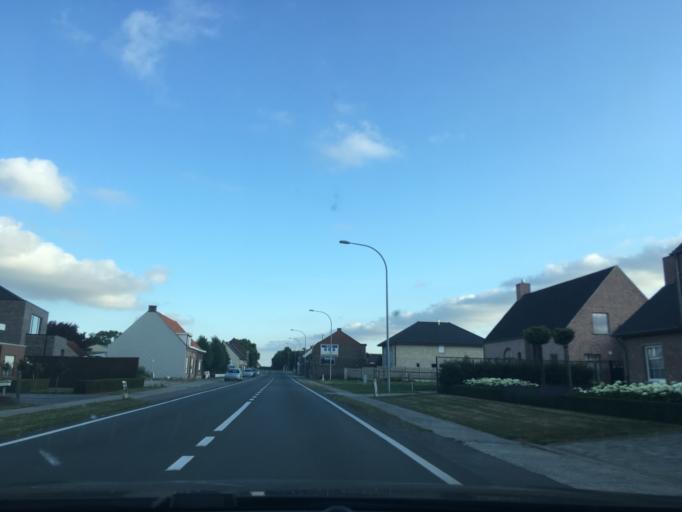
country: BE
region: Flanders
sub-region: Provincie West-Vlaanderen
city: Wingene
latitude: 51.0329
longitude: 3.3042
